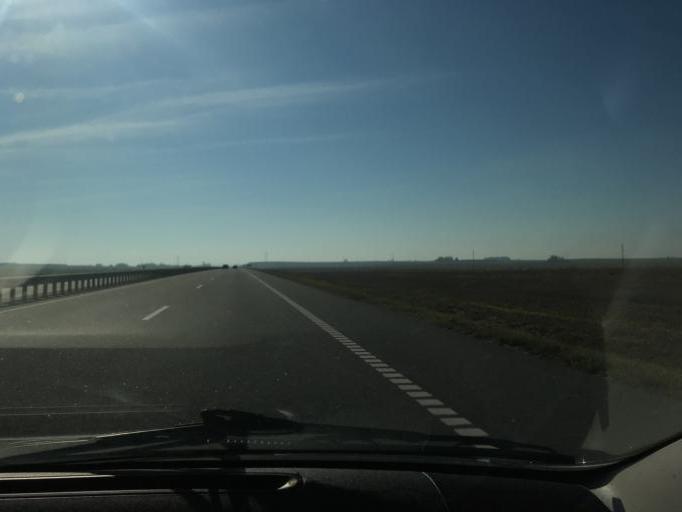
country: BY
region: Minsk
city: Slutsk
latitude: 53.1972
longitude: 27.5509
